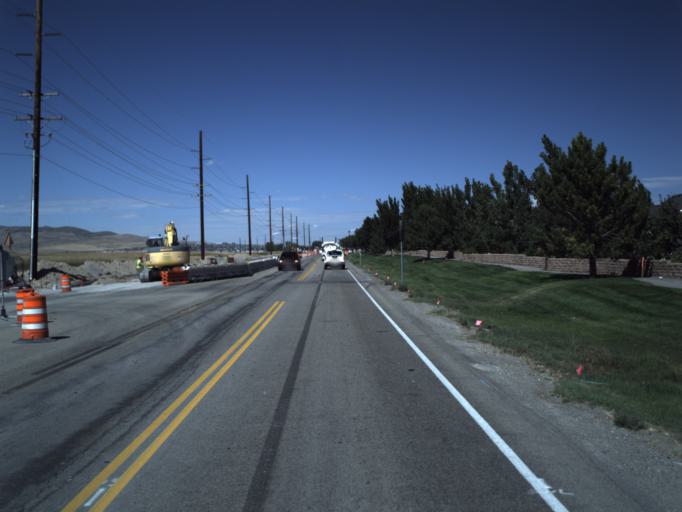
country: US
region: Utah
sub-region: Utah County
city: Saratoga Springs
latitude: 40.3409
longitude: -111.9160
